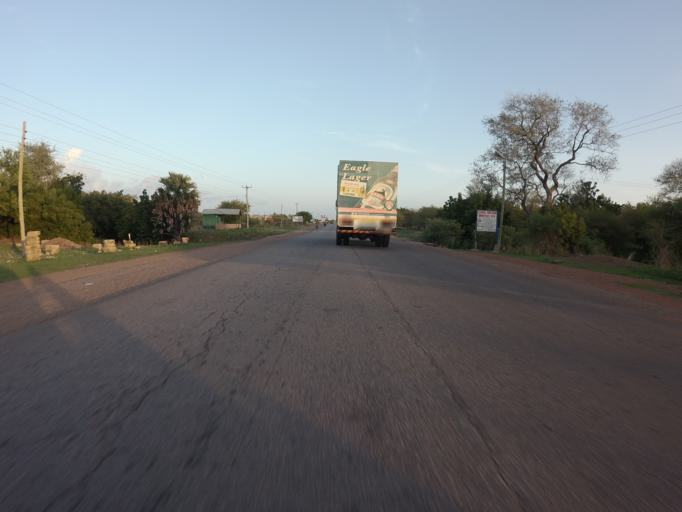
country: GH
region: Upper East
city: Navrongo
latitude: 10.9604
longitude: -1.0990
